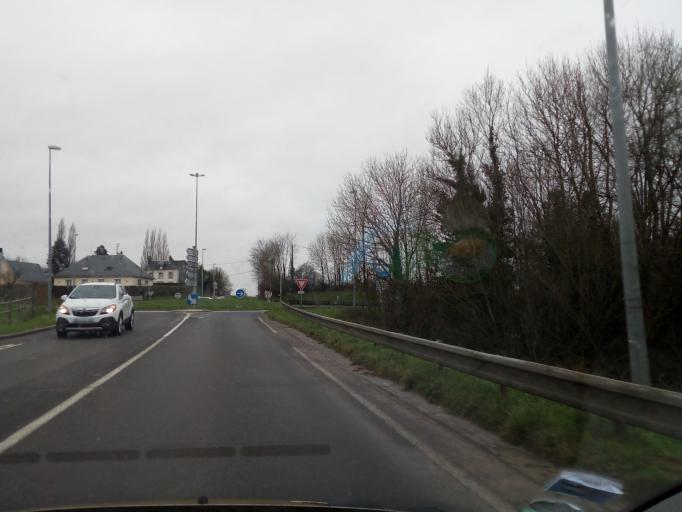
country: FR
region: Haute-Normandie
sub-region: Departement de la Seine-Maritime
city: Auzebosc
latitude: 49.6062
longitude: 0.7410
